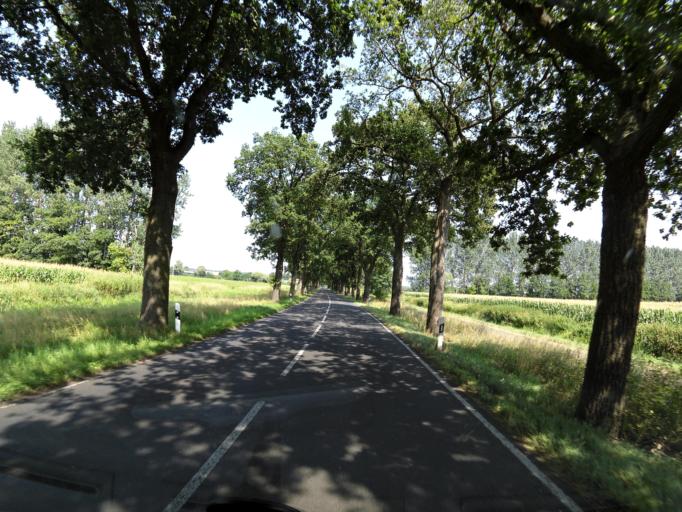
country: DE
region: Brandenburg
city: Liebenwalde
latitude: 52.8754
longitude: 13.3424
